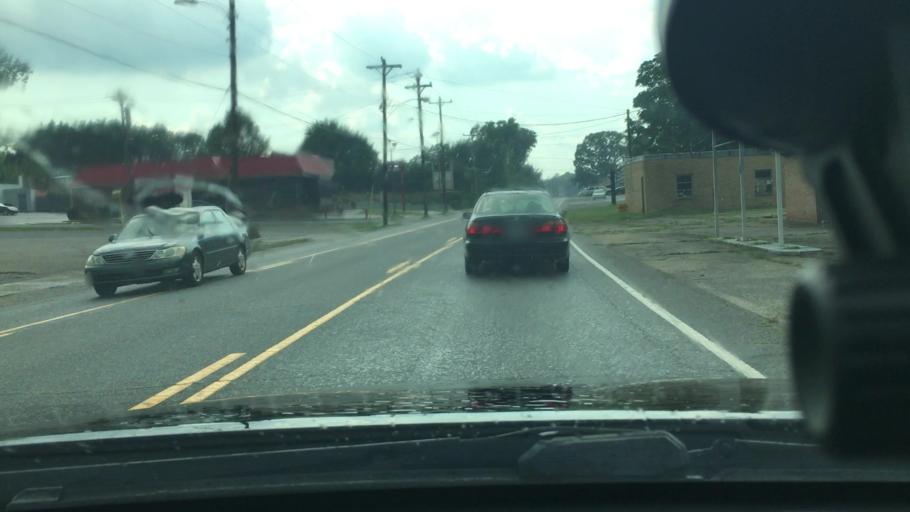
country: US
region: North Carolina
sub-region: Rutherford County
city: Spindale
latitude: 35.3589
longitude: -81.9345
